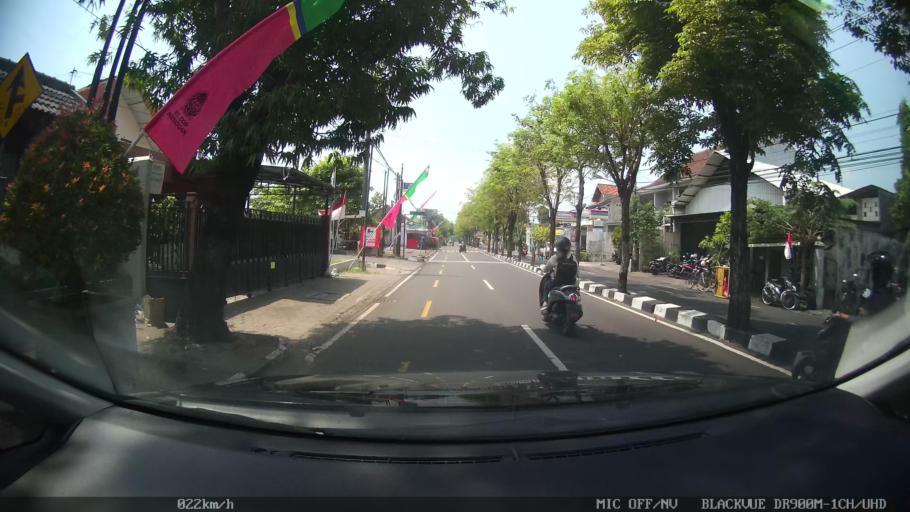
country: ID
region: Daerah Istimewa Yogyakarta
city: Yogyakarta
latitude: -7.8192
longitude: 110.3957
